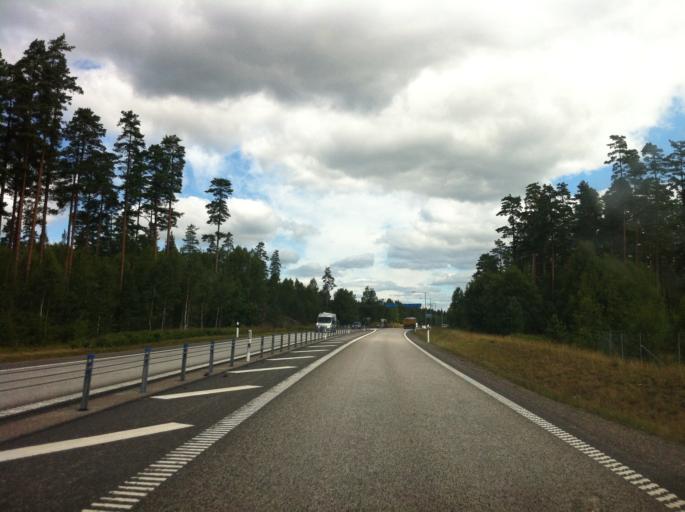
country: SE
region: Joenkoeping
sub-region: Gislaveds Kommun
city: Gislaved
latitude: 57.3384
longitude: 13.5496
